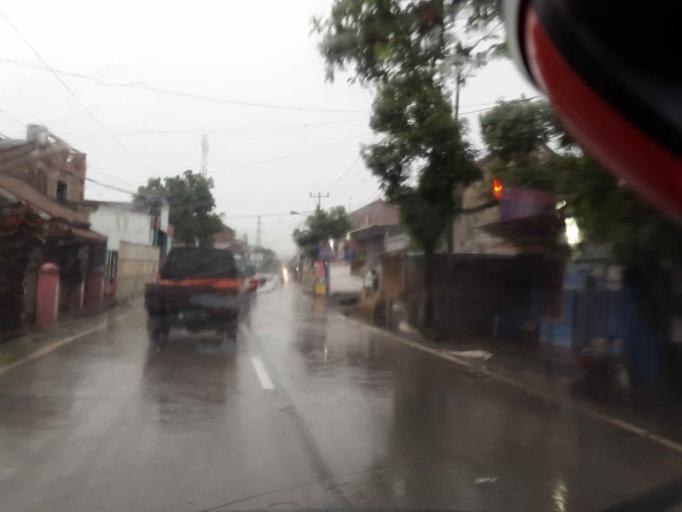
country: ID
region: West Java
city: Cimahi
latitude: -6.9239
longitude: 107.4955
